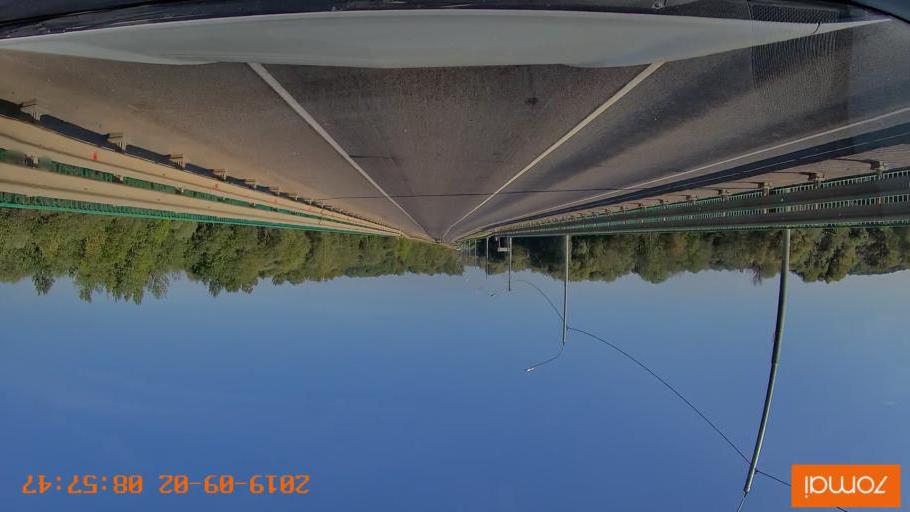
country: RU
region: Kaluga
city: Myatlevo
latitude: 54.9339
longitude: 35.7600
